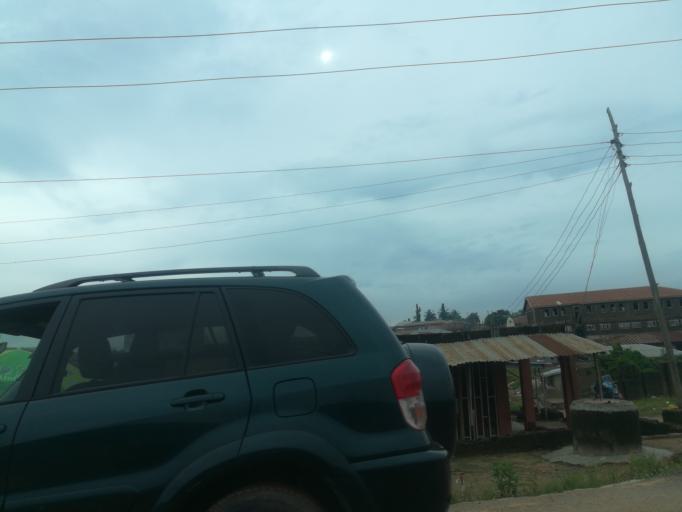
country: NG
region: Oyo
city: Egbeda
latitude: 7.3769
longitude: 3.9961
